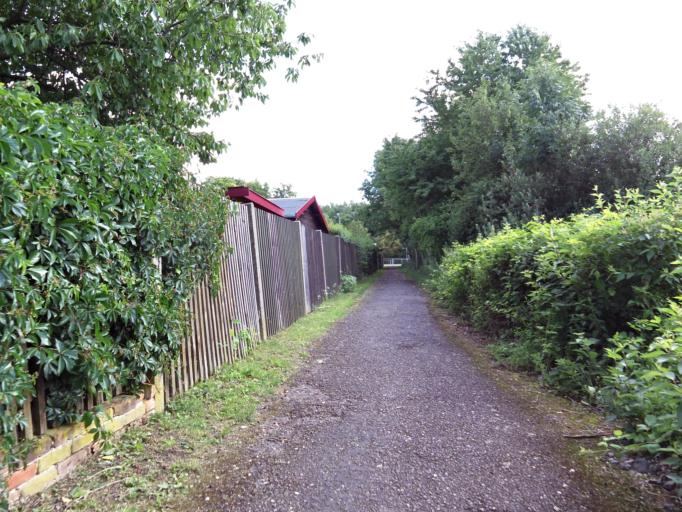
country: DE
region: Saxony
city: Leipzig
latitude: 51.3316
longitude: 12.4313
